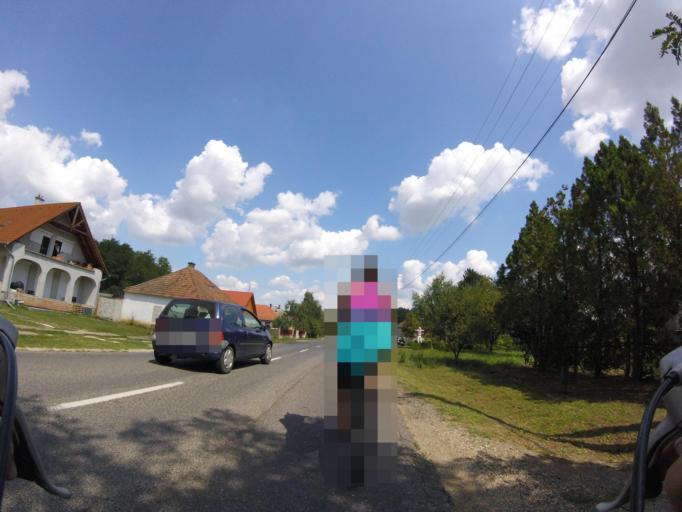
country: HU
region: Gyor-Moson-Sopron
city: Tet
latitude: 47.4918
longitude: 17.4977
